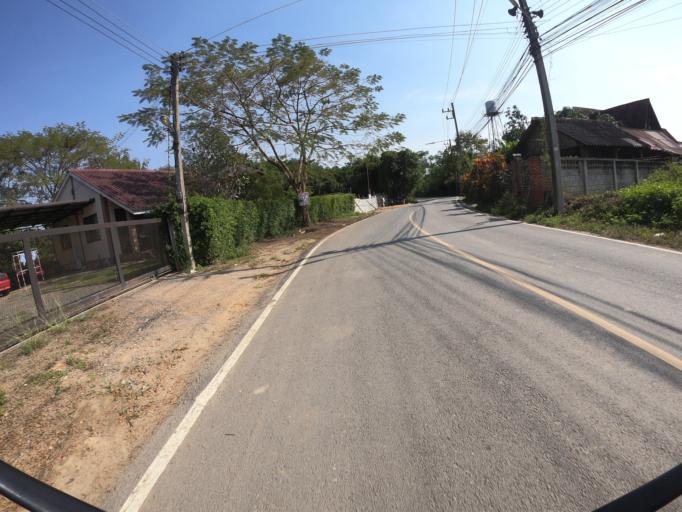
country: TH
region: Chiang Mai
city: San Sai
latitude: 18.8460
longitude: 99.0016
